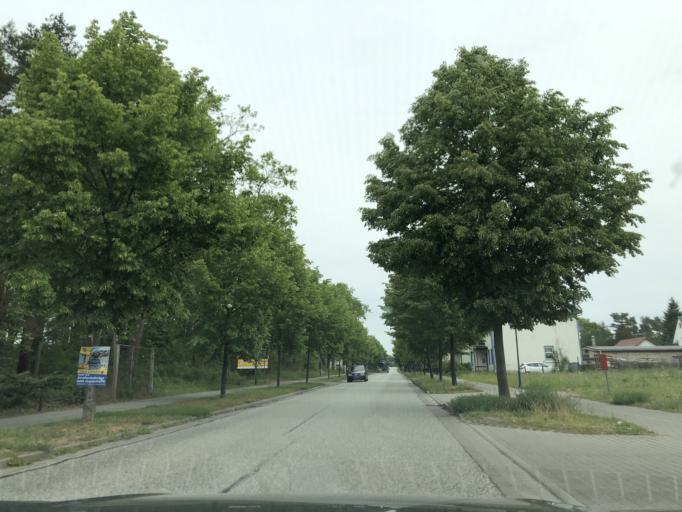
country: DE
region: Brandenburg
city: Plattenburg
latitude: 52.9126
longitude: 12.0854
